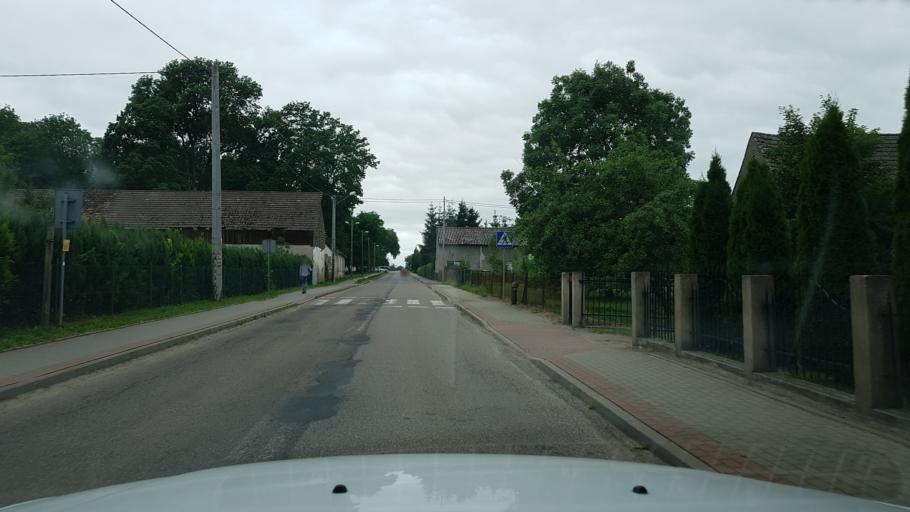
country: PL
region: West Pomeranian Voivodeship
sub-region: Powiat gryficki
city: Brojce
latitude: 53.9572
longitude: 15.3607
